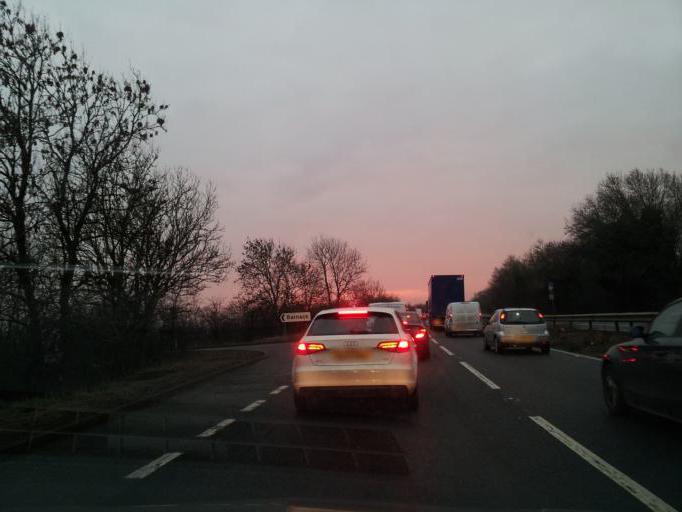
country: GB
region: England
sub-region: Peterborough
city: Wittering
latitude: 52.6095
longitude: -0.4343
